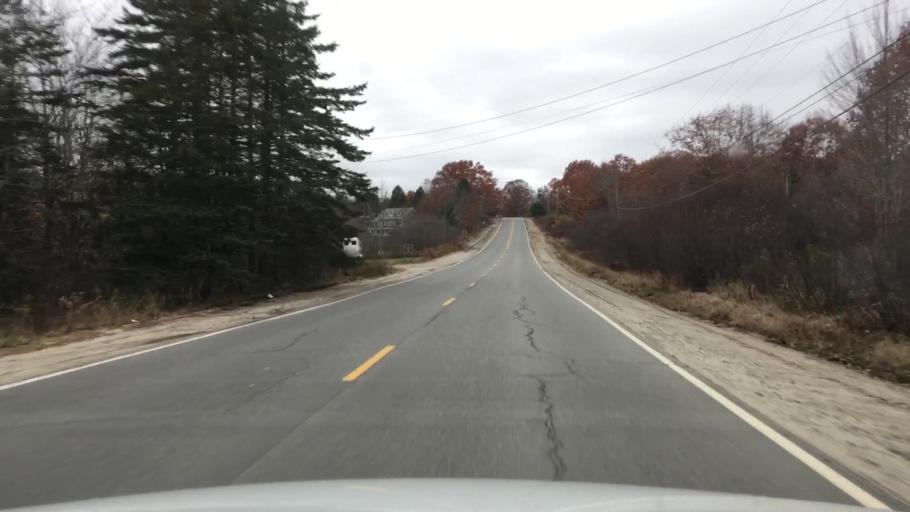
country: US
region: Maine
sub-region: Hancock County
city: Sedgwick
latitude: 44.3889
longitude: -68.5778
